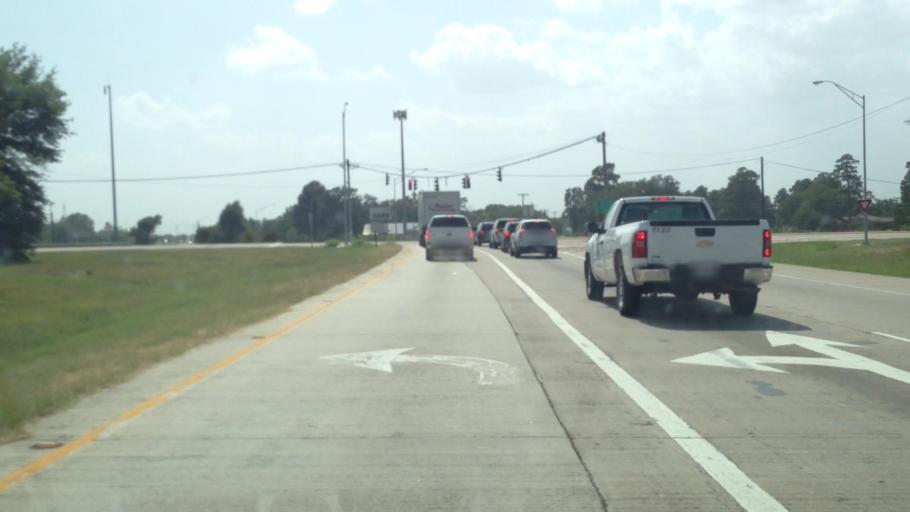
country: US
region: Louisiana
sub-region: Caddo Parish
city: Greenwood
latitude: 32.4514
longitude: -93.8646
